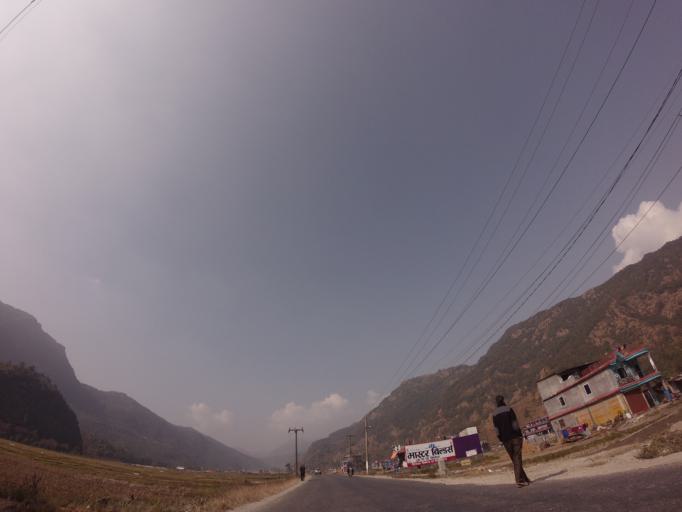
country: NP
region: Western Region
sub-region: Gandaki Zone
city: Pokhara
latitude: 28.2832
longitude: 83.9223
